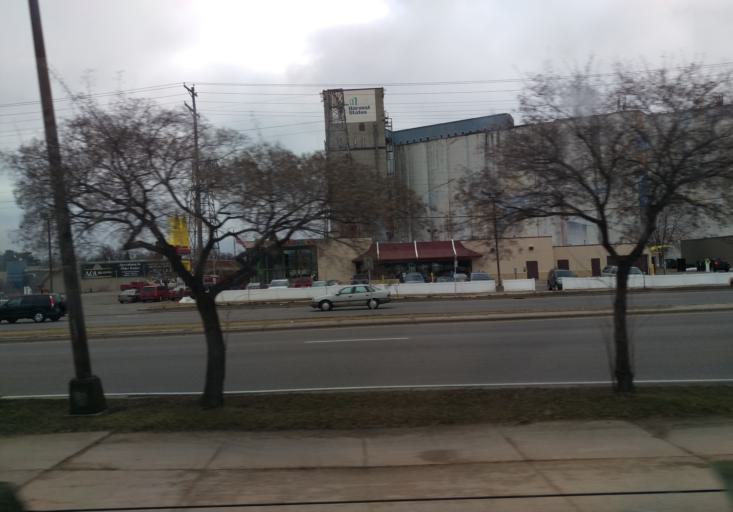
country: US
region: Minnesota
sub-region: Hennepin County
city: Minneapolis
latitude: 44.9281
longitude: -93.2248
